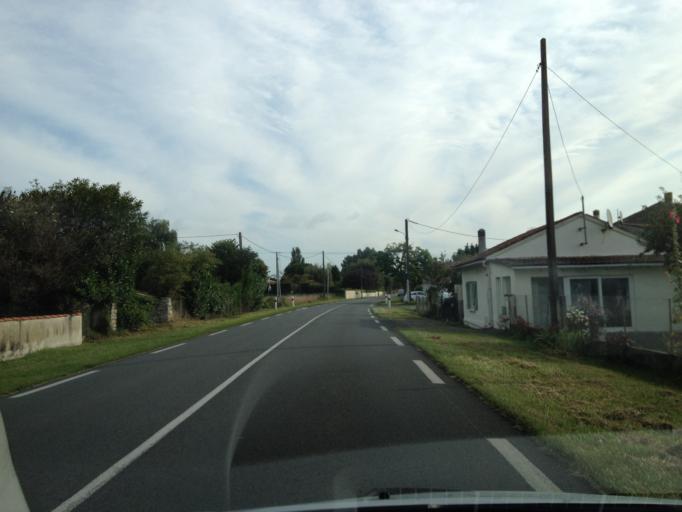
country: FR
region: Poitou-Charentes
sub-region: Departement de la Charente-Maritime
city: Le Gua
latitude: 45.7264
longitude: -0.9626
